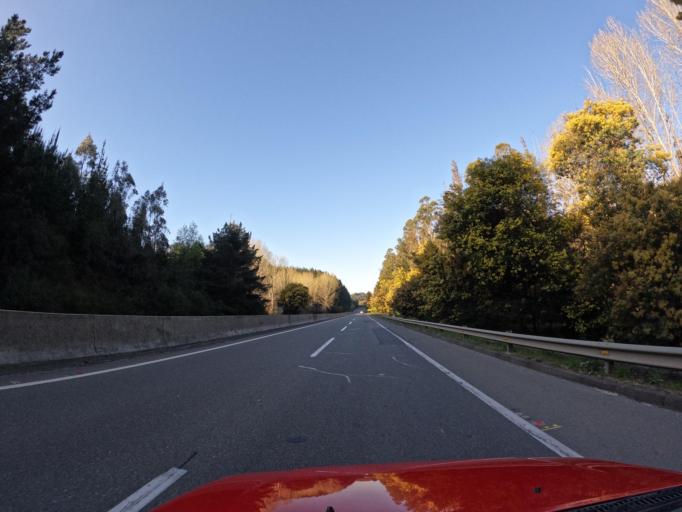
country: CL
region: Biobio
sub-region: Provincia de Concepcion
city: Penco
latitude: -36.7304
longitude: -72.8454
